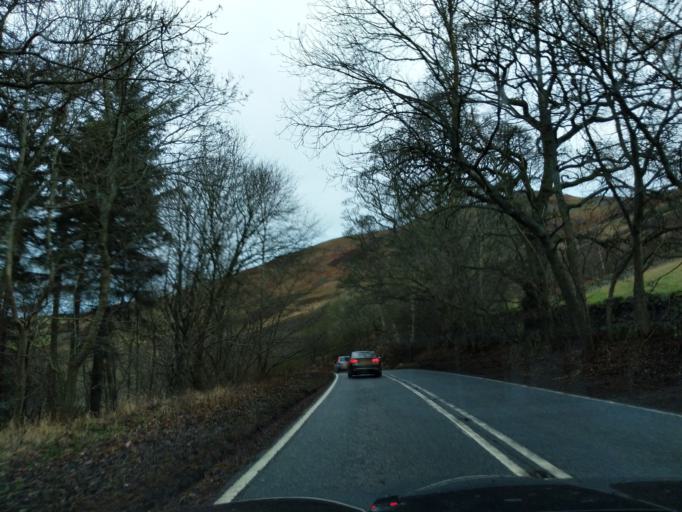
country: GB
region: Scotland
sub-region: The Scottish Borders
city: Galashiels
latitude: 55.6615
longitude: -2.8602
